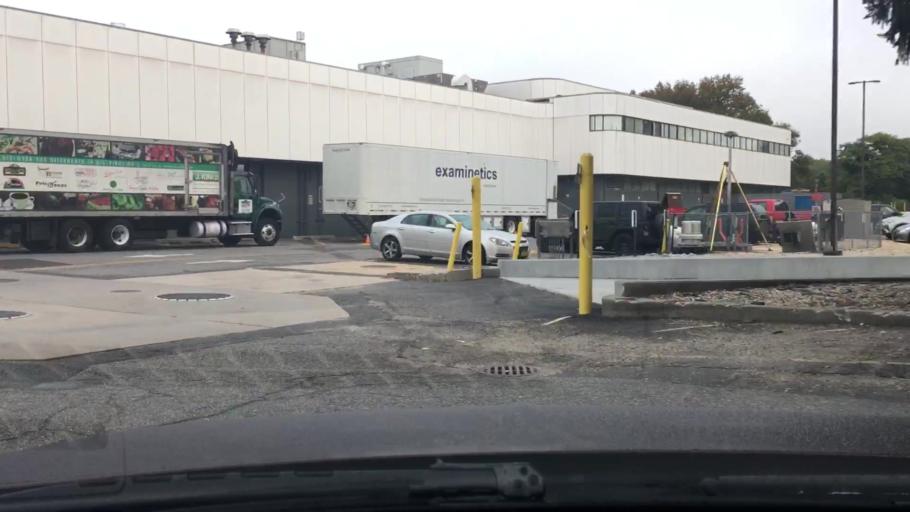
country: US
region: New York
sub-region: Suffolk County
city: Melville
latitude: 40.7799
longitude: -73.4078
